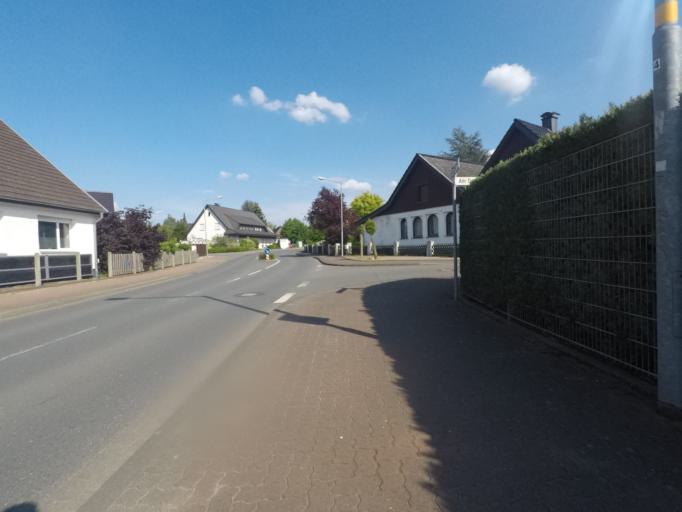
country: DE
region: North Rhine-Westphalia
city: Loehne
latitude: 52.1848
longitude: 8.6713
